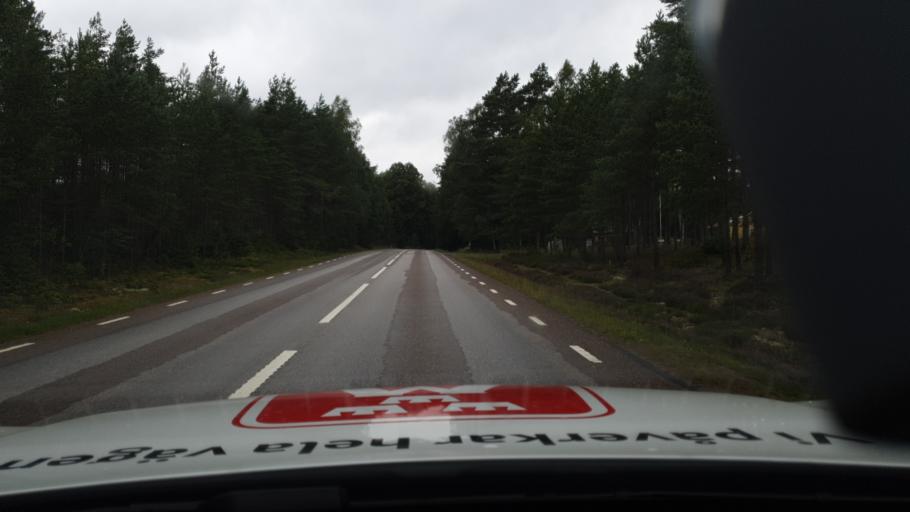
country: SE
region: Vaestra Goetaland
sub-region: Lilla Edets Kommun
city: Lilla Edet
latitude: 58.1682
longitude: 12.0258
